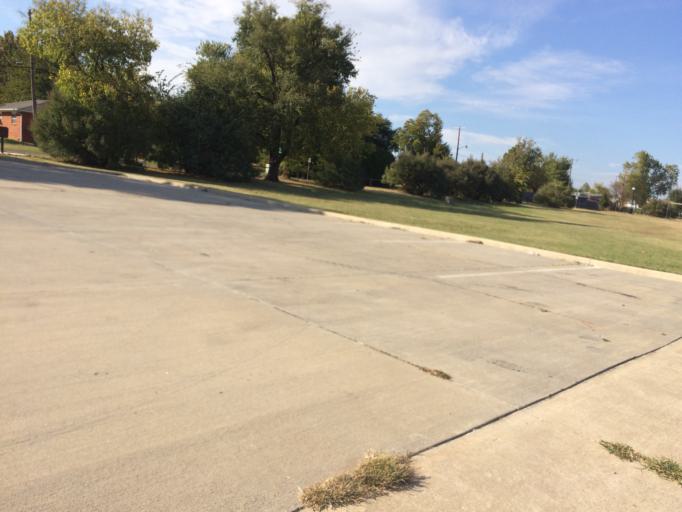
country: US
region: Oklahoma
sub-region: Cleveland County
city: Norman
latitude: 35.2308
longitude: -97.4319
